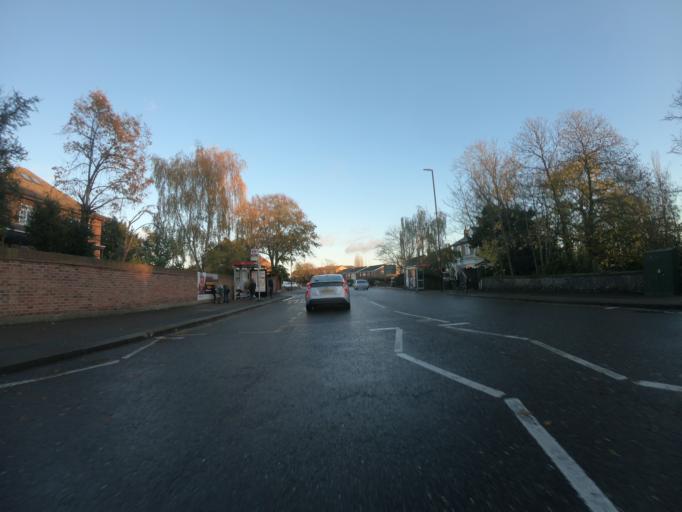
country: GB
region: England
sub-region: Greater London
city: Belvedere
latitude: 51.4842
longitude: 0.1485
